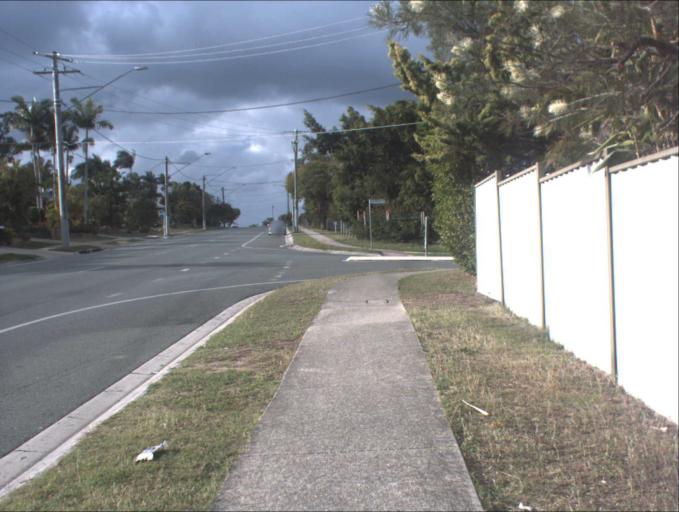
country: AU
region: Queensland
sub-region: Logan
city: Park Ridge South
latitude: -27.6792
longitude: 153.0370
